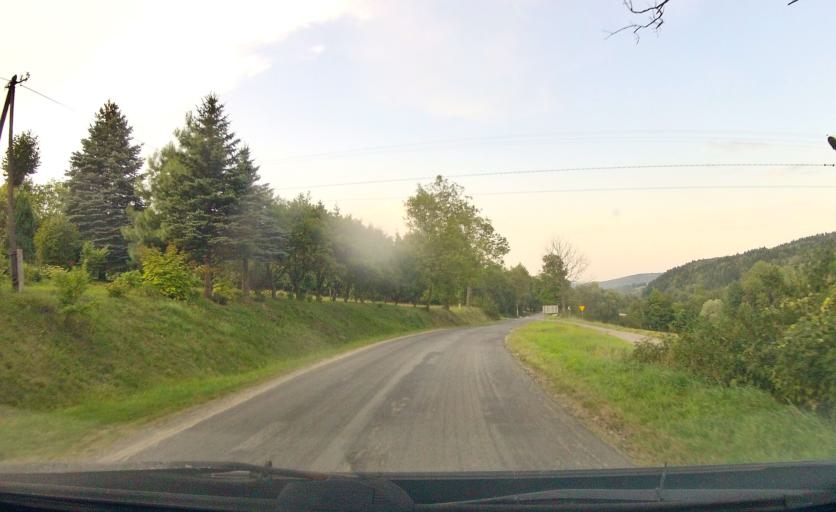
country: PL
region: Subcarpathian Voivodeship
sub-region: Powiat krosnienski
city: Dukla
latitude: 49.5334
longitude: 21.6152
